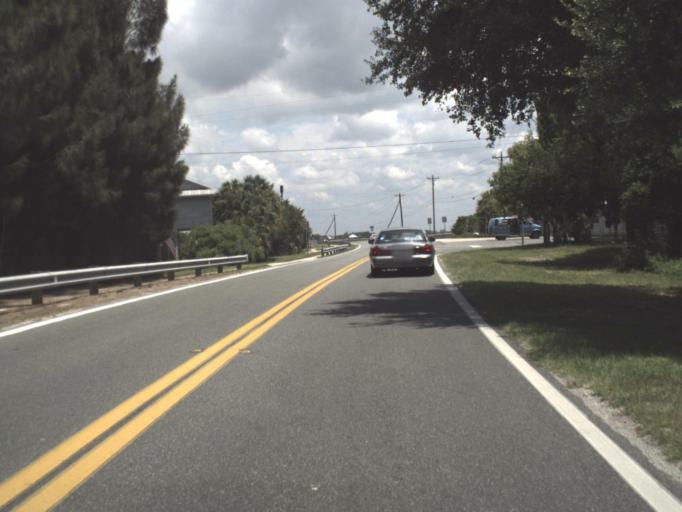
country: US
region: Florida
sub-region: Levy County
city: Chiefland
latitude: 29.1478
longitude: -83.0324
